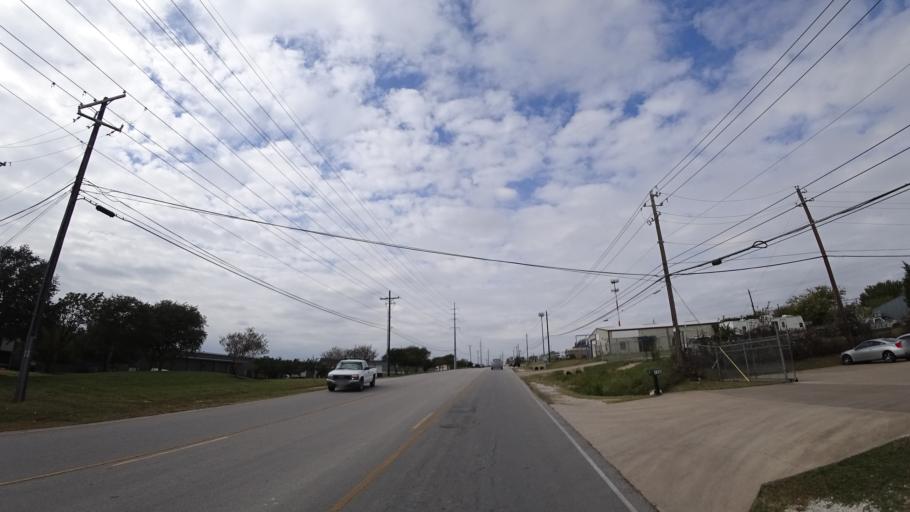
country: US
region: Texas
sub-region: Travis County
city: Wells Branch
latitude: 30.4294
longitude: -97.6818
